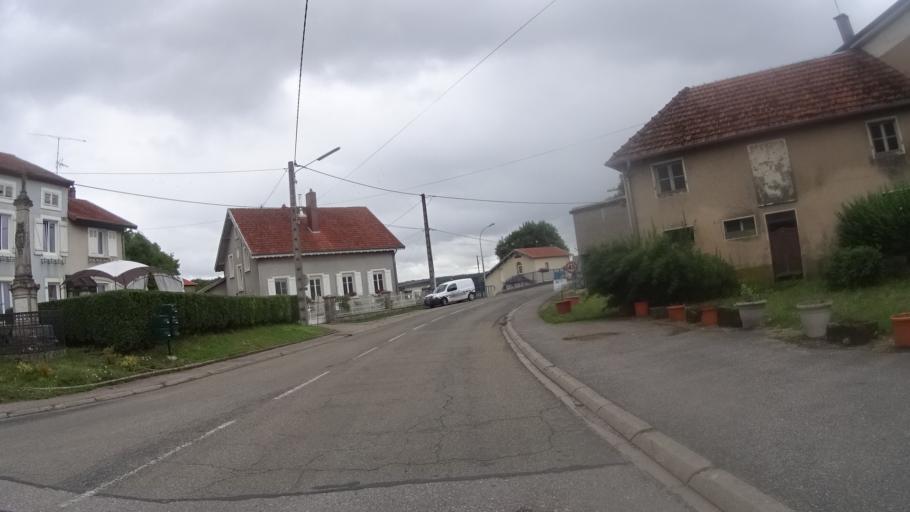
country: FR
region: Lorraine
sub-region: Departement de la Moselle
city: Dieuze
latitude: 48.6908
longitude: 6.7099
